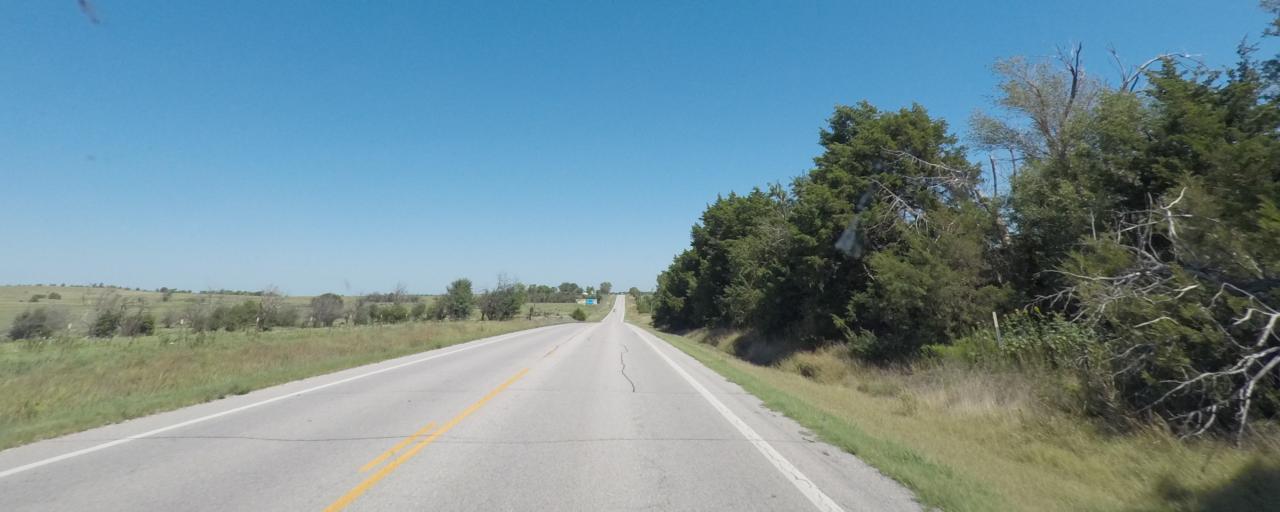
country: US
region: Kansas
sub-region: Sumner County
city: Wellington
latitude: 37.2232
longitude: -97.4026
